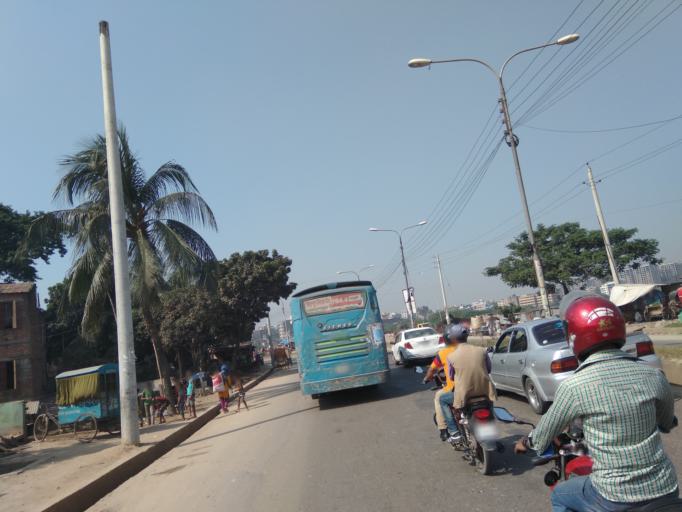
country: BD
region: Dhaka
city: Tungi
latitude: 23.8231
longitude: 90.3807
